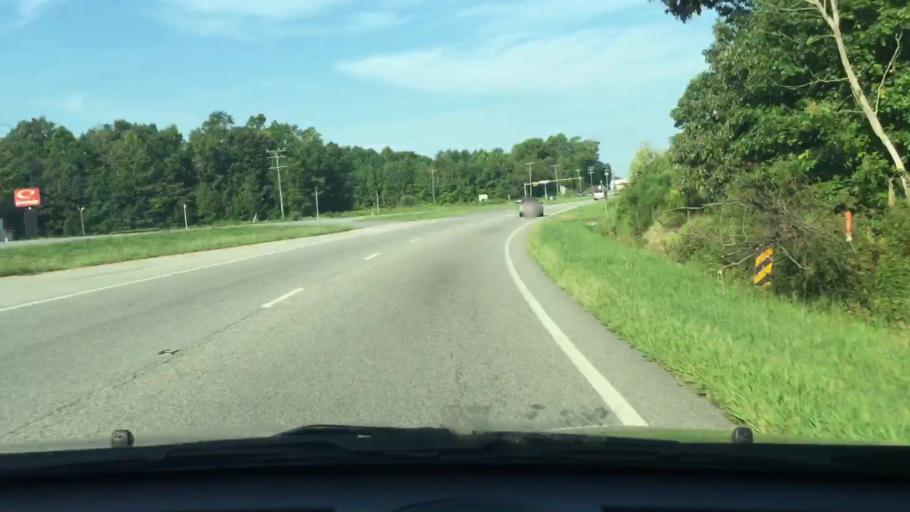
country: US
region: Virginia
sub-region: Isle of Wight County
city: Carrollton
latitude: 36.9387
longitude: -76.5771
